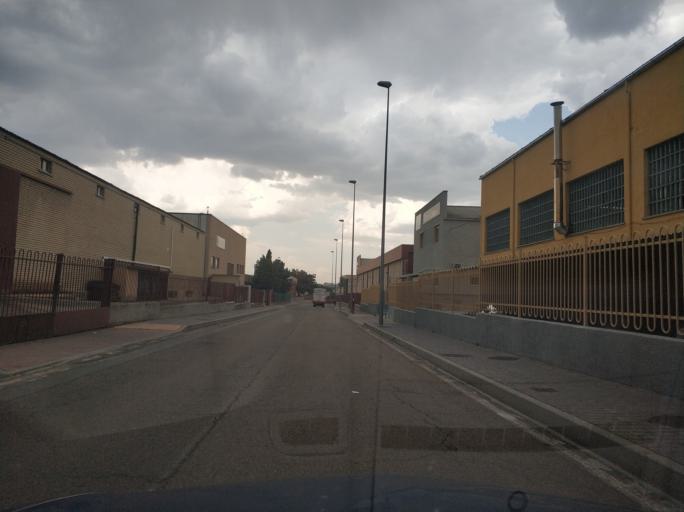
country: ES
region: Castille and Leon
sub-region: Provincia de Salamanca
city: Carbajosa de la Sagrada
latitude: 40.9428
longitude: -5.6625
